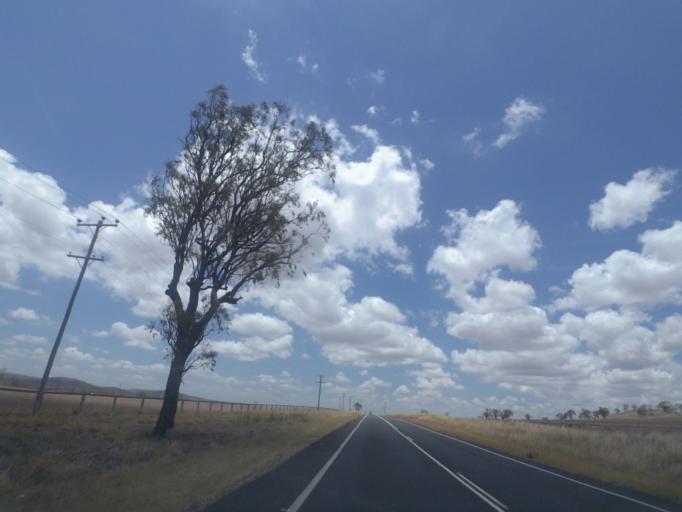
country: AU
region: Queensland
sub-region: Toowoomba
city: Top Camp
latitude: -27.7461
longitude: 151.9284
